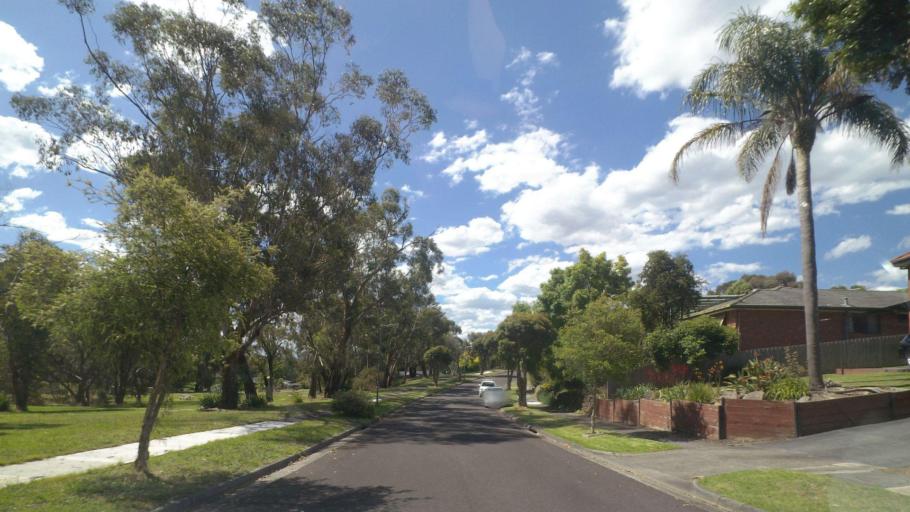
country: AU
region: Victoria
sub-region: Yarra Ranges
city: Kilsyth
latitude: -37.8067
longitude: 145.3292
